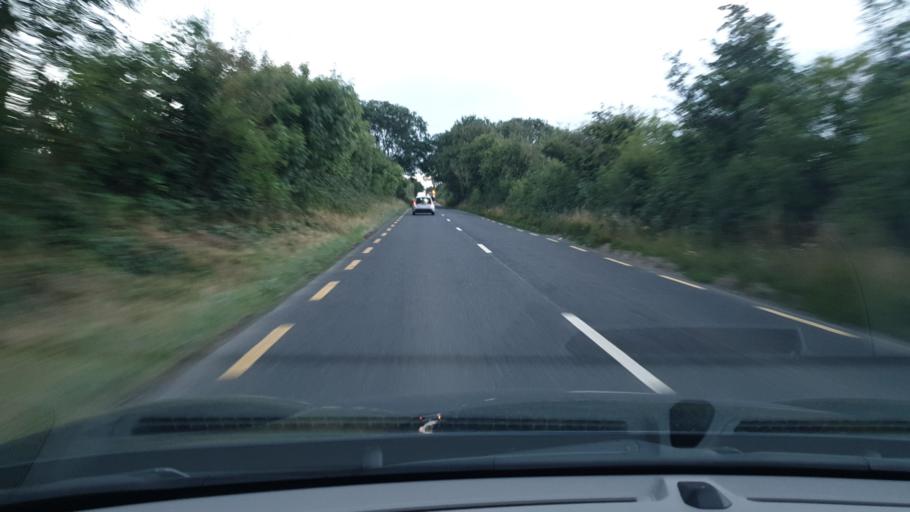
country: IE
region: Leinster
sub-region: An Mhi
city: Duleek
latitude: 53.6113
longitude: -6.4313
